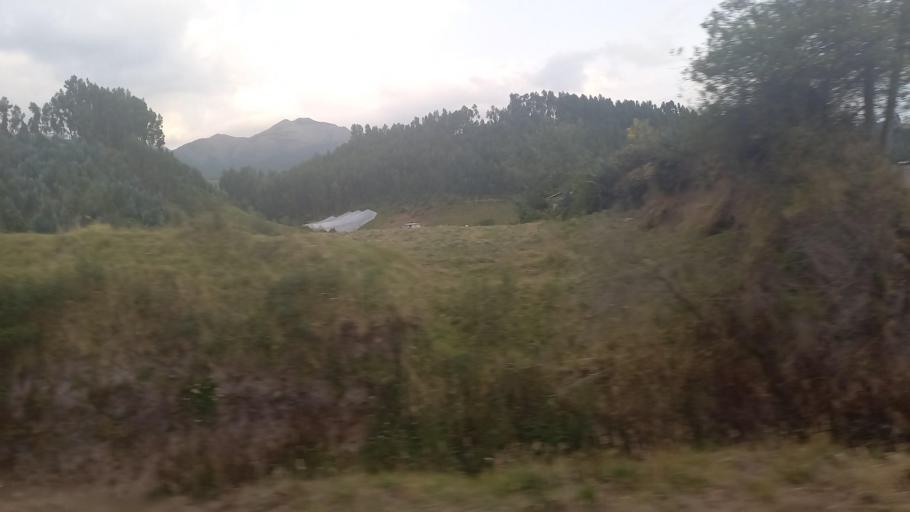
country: EC
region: Pichincha
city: Cayambe
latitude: 0.0819
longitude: -78.1064
